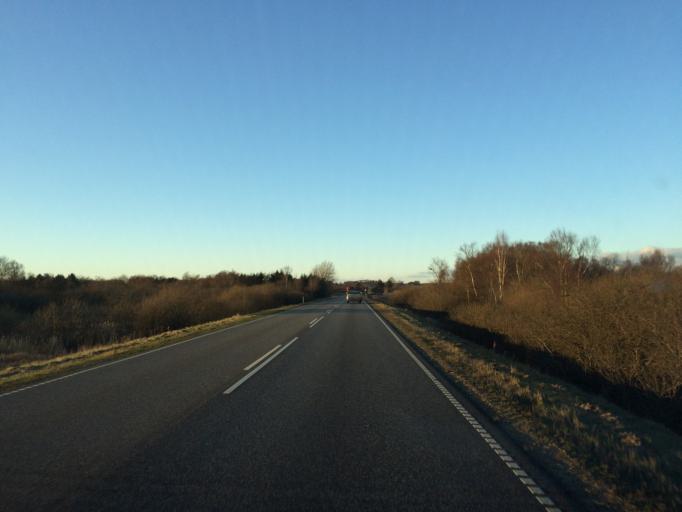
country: DK
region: Central Jutland
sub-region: Randers Kommune
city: Langa
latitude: 56.4904
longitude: 9.8582
